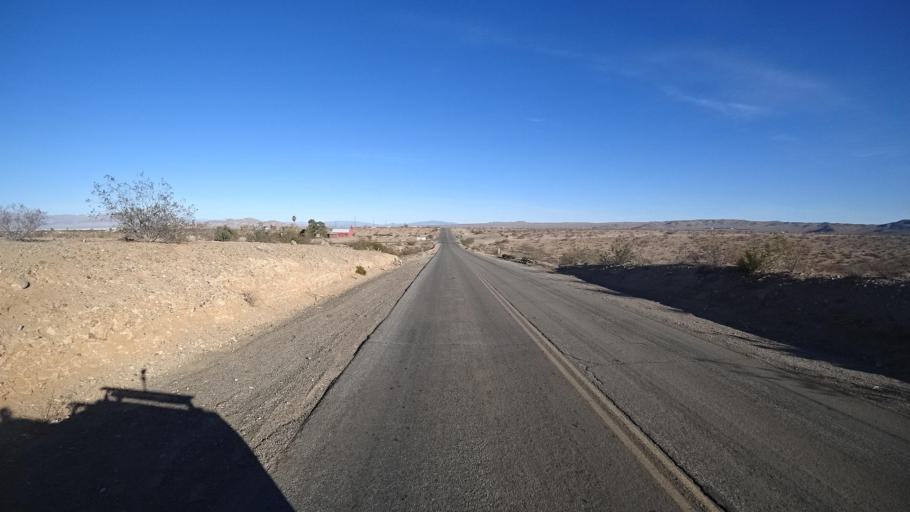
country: US
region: California
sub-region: Kern County
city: China Lake Acres
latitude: 35.6079
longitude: -117.7251
